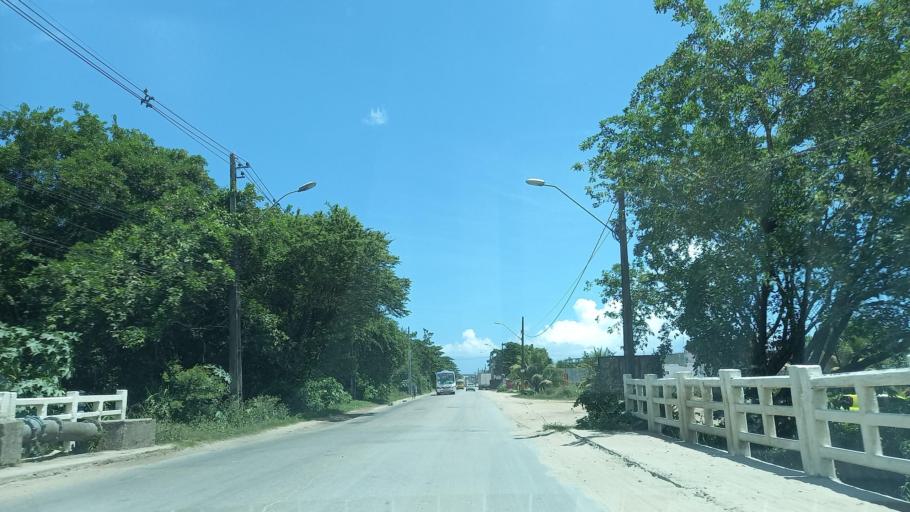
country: BR
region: Pernambuco
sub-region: Jaboatao Dos Guararapes
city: Jaboatao
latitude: -8.1586
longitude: -34.9758
